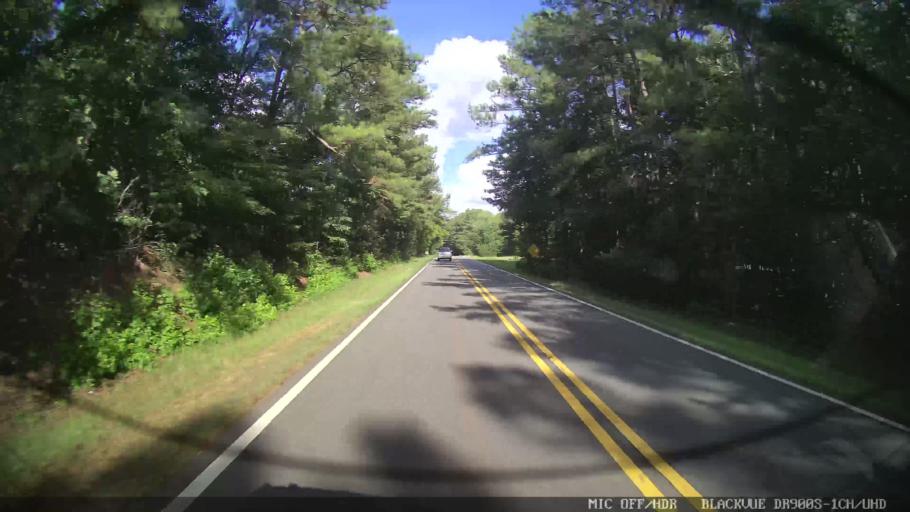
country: US
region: Georgia
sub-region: Bartow County
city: Euharlee
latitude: 34.1805
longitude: -85.0277
